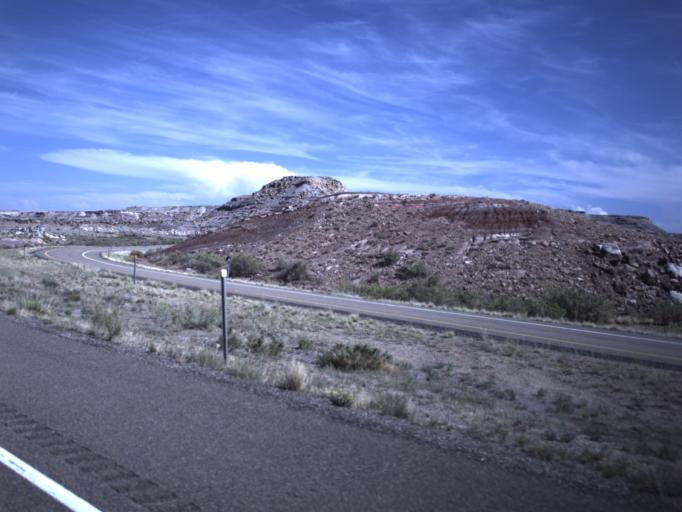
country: US
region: Utah
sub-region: Carbon County
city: East Carbon City
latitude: 38.9217
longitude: -110.3816
